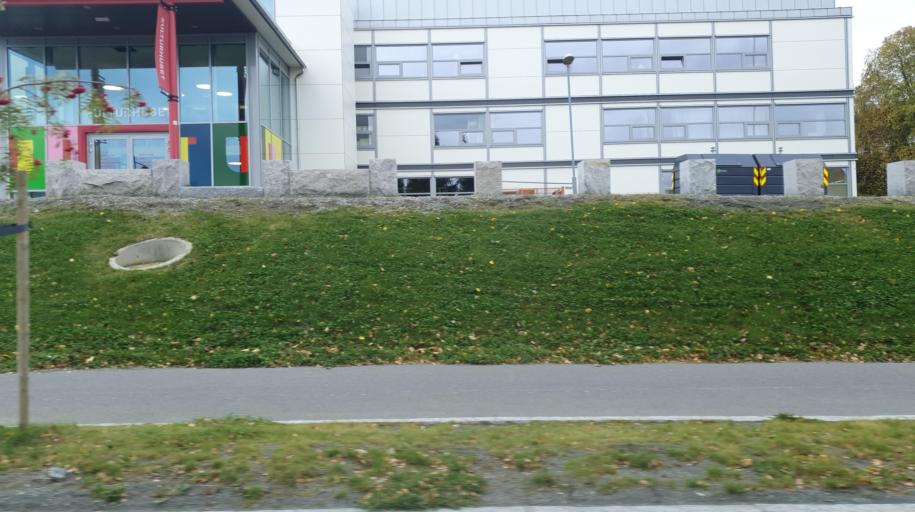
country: NO
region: Sor-Trondelag
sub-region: Klaebu
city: Klaebu
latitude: 63.2997
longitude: 10.4849
